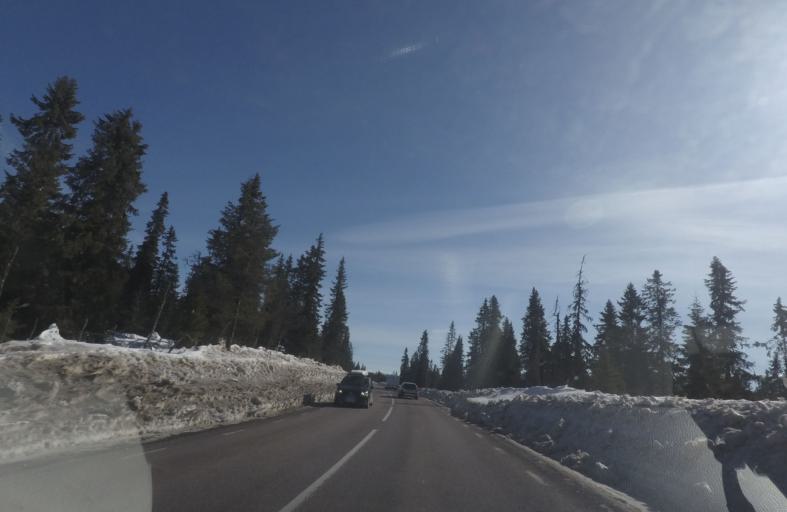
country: SE
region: Dalarna
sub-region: Malung-Saelens kommun
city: Malung
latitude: 61.1745
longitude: 13.0700
